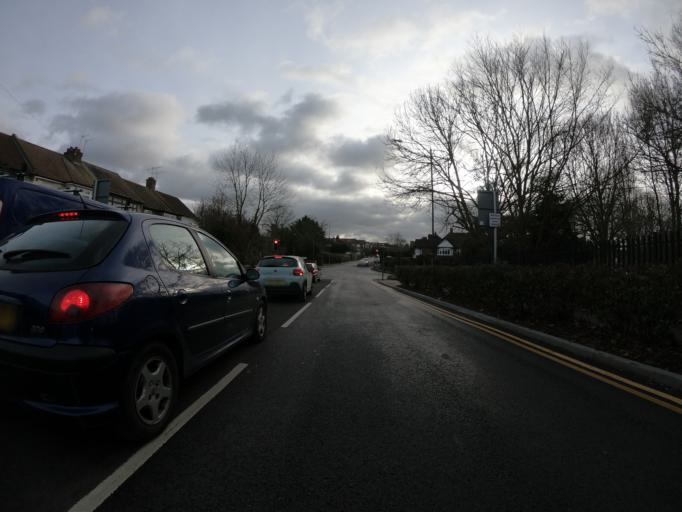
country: GB
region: England
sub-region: Kent
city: Gravesend
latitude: 51.4305
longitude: 0.3646
